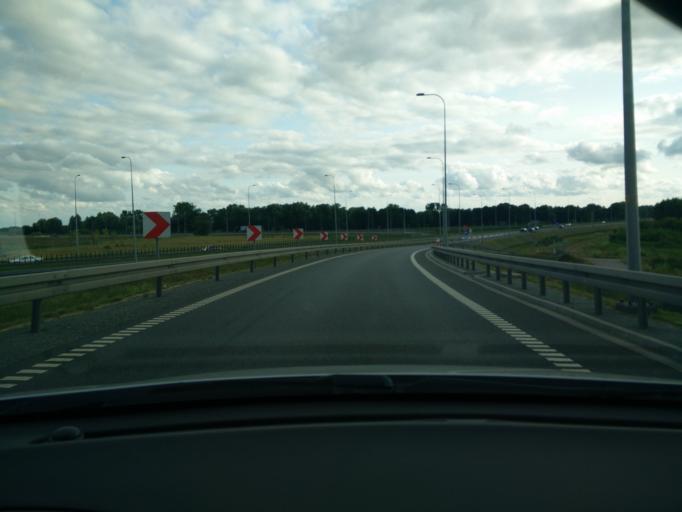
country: PL
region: Pomeranian Voivodeship
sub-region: Gdansk
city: Gdansk
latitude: 54.3201
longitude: 18.7044
